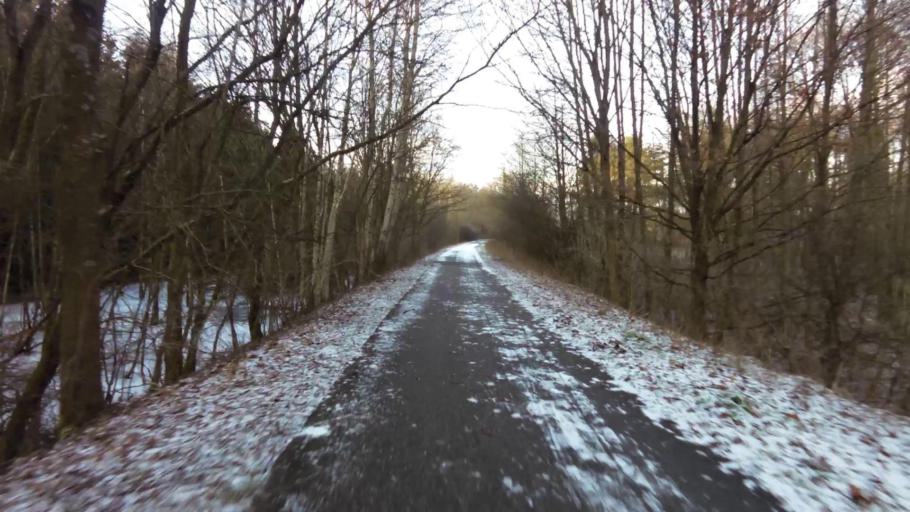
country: PL
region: West Pomeranian Voivodeship
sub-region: Powiat drawski
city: Zlocieniec
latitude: 53.5802
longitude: 16.0403
